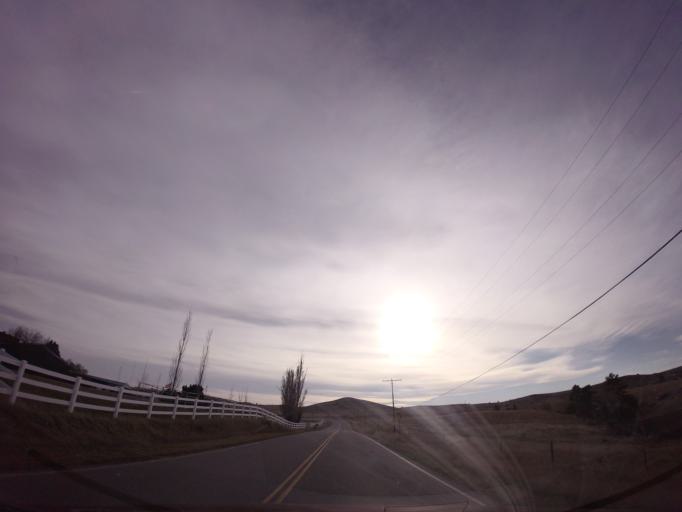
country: US
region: Montana
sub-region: Yellowstone County
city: Billings
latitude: 45.7782
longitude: -108.4621
